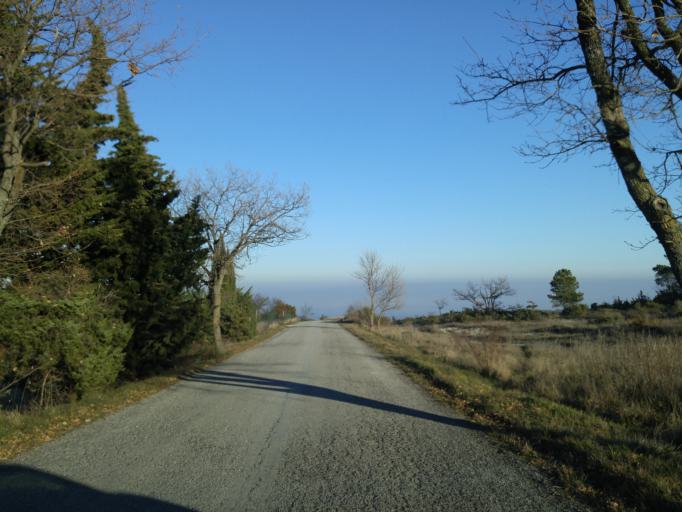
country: IT
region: The Marches
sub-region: Provincia di Pesaro e Urbino
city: Isola del Piano
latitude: 43.7139
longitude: 12.7446
